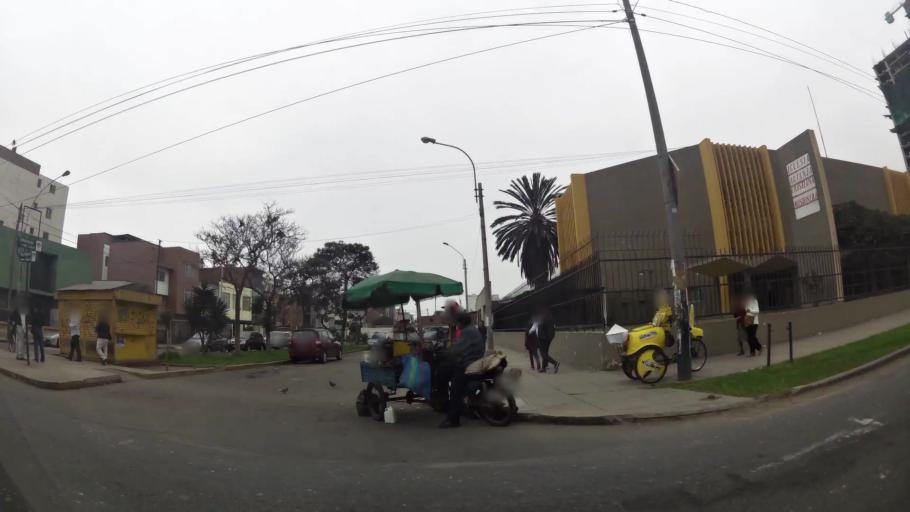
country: PE
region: Lima
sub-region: Lima
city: San Isidro
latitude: -12.0780
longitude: -77.0563
